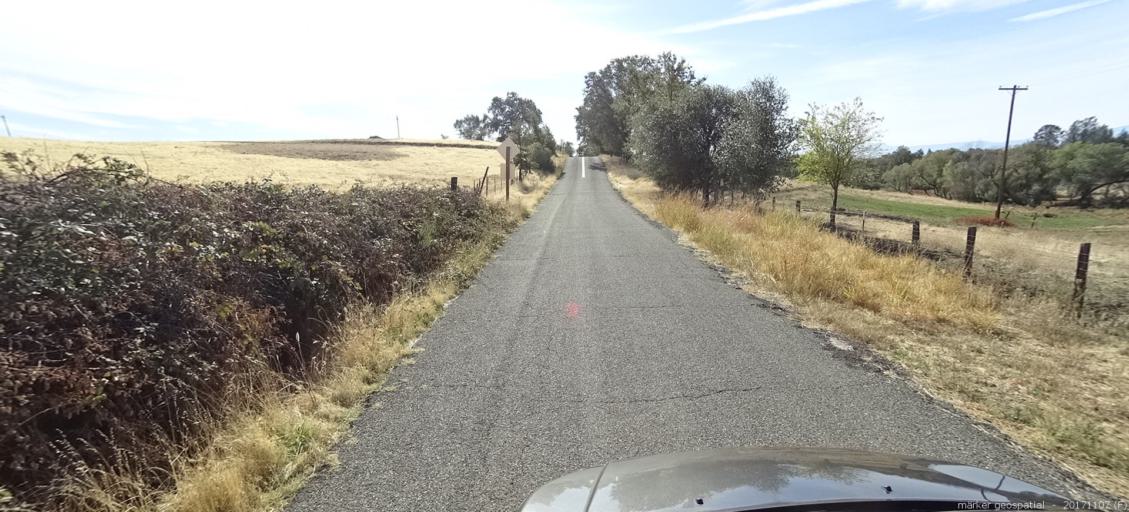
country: US
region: California
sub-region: Shasta County
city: Shasta
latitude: 40.5074
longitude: -122.5470
